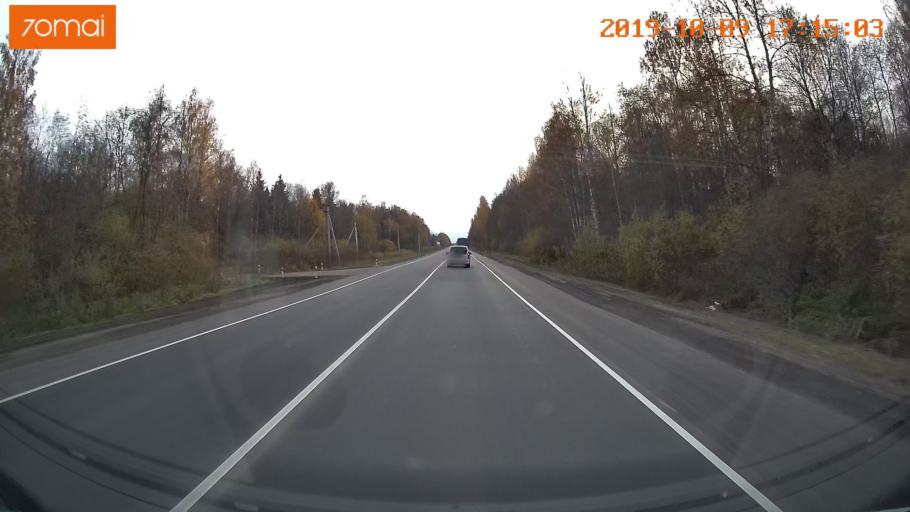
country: RU
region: Ivanovo
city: Furmanov
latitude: 57.3005
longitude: 41.1978
